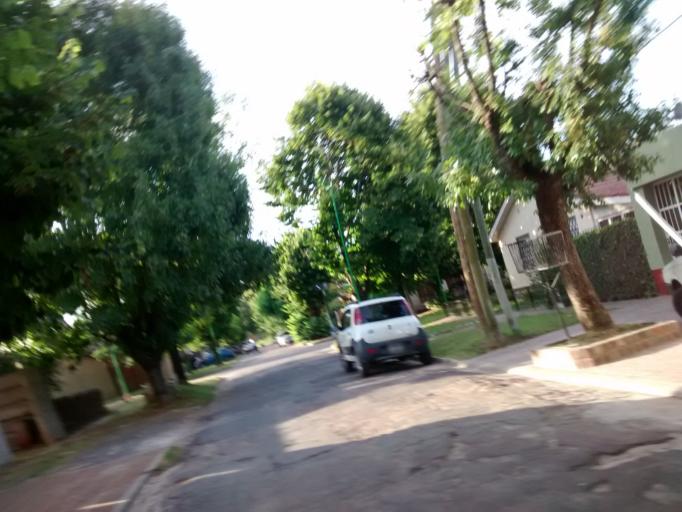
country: AR
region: Buenos Aires
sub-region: Partido de La Plata
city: La Plata
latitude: -34.8713
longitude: -58.0873
